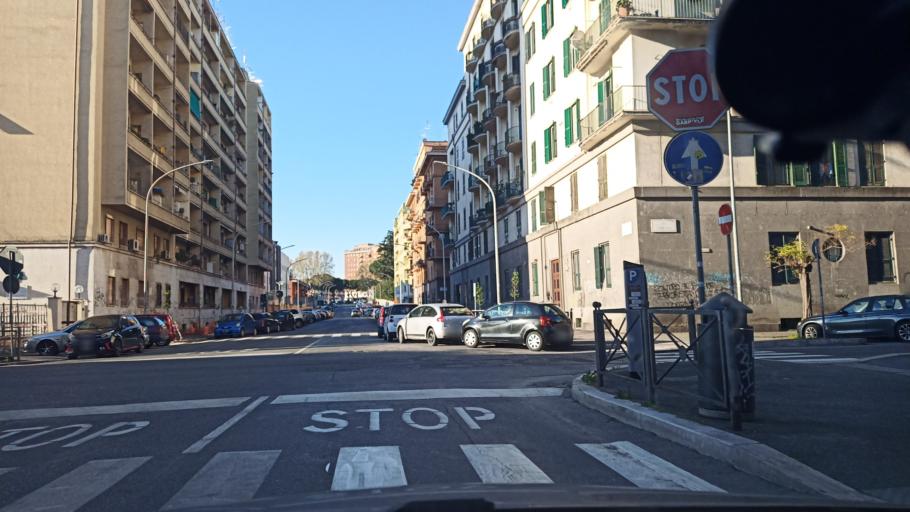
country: IT
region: Latium
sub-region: Citta metropolitana di Roma Capitale
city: Rome
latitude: 41.8796
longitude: 12.5113
